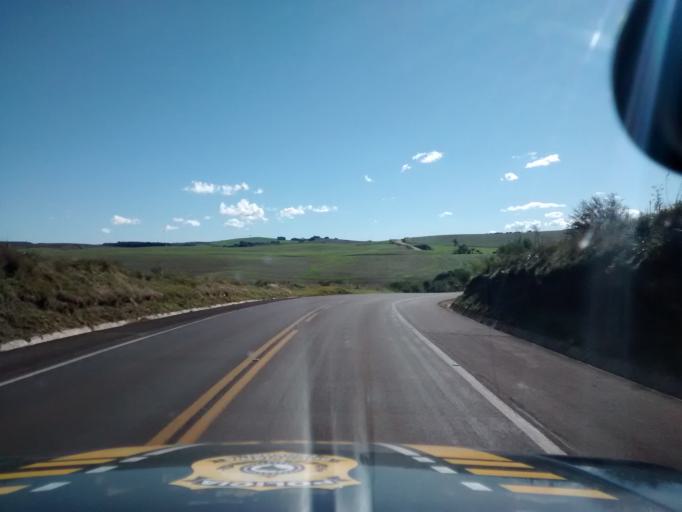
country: BR
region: Rio Grande do Sul
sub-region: Lagoa Vermelha
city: Lagoa Vermelha
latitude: -28.3196
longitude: -51.3467
